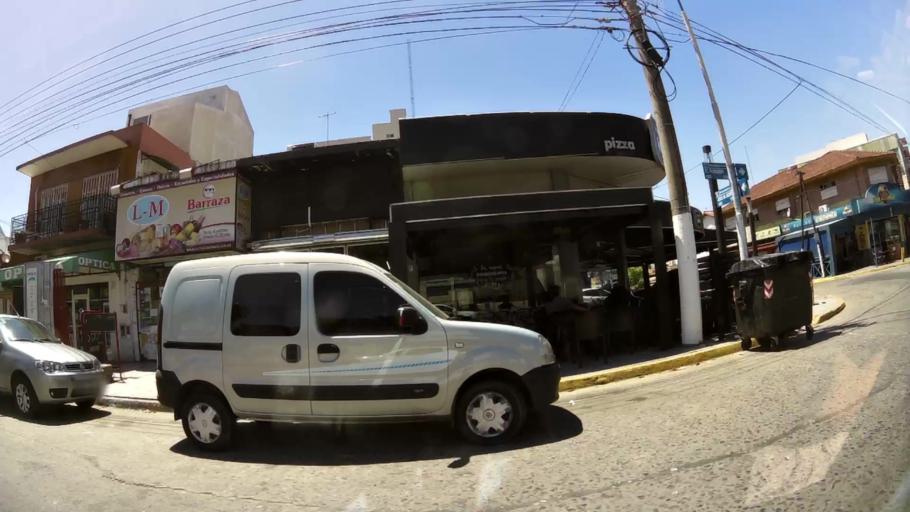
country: AR
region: Buenos Aires
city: Caseros
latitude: -34.5898
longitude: -58.5715
